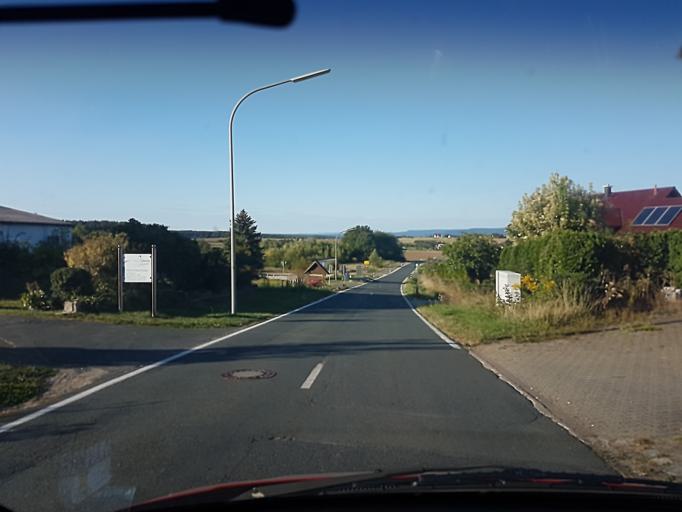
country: DE
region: Bavaria
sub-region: Upper Franconia
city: Hallerndorf
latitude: 49.7721
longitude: 10.9486
